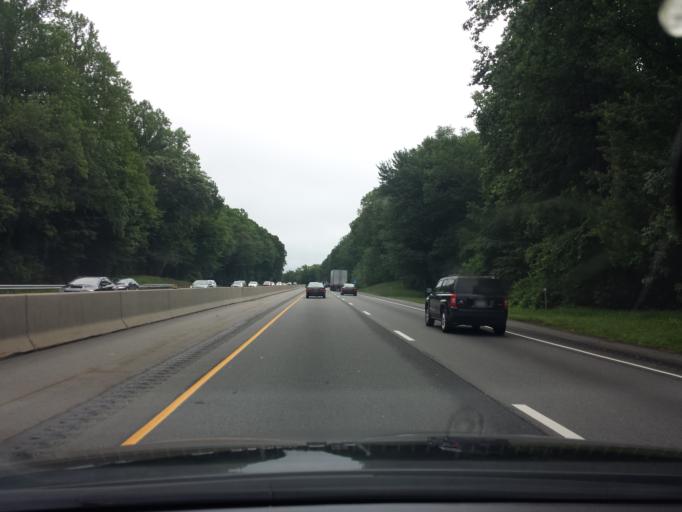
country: US
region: Connecticut
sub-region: Middlesex County
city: Westbrook Center
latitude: 41.2923
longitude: -72.4742
